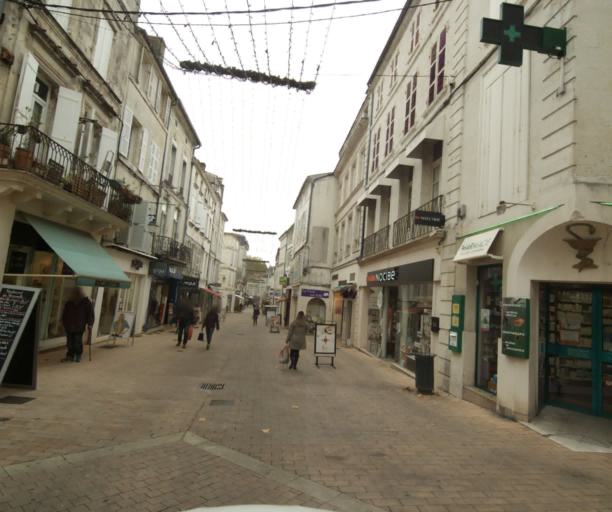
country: FR
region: Poitou-Charentes
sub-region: Departement de la Charente-Maritime
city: Saintes
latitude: 45.7468
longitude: -0.6335
